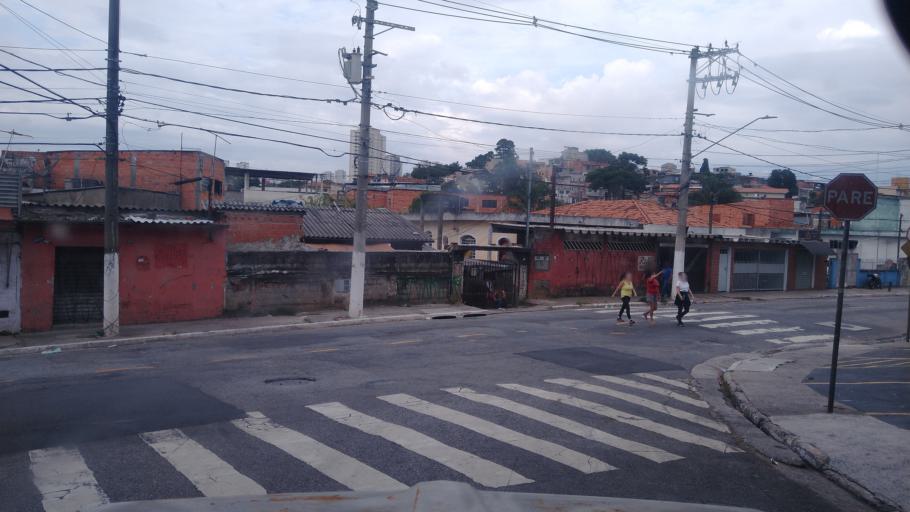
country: BR
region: Sao Paulo
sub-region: Taboao Da Serra
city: Taboao da Serra
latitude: -23.6273
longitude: -46.7614
